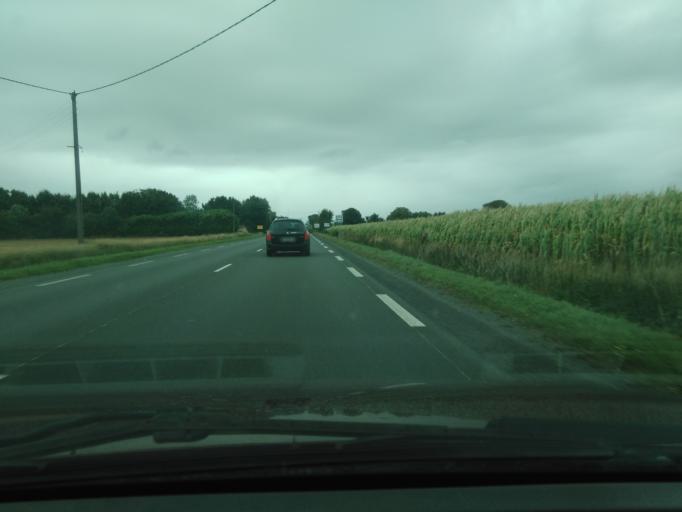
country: FR
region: Pays de la Loire
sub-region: Departement de la Vendee
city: Sainte-Gemme-la-Plaine
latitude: 46.4596
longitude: -1.1064
